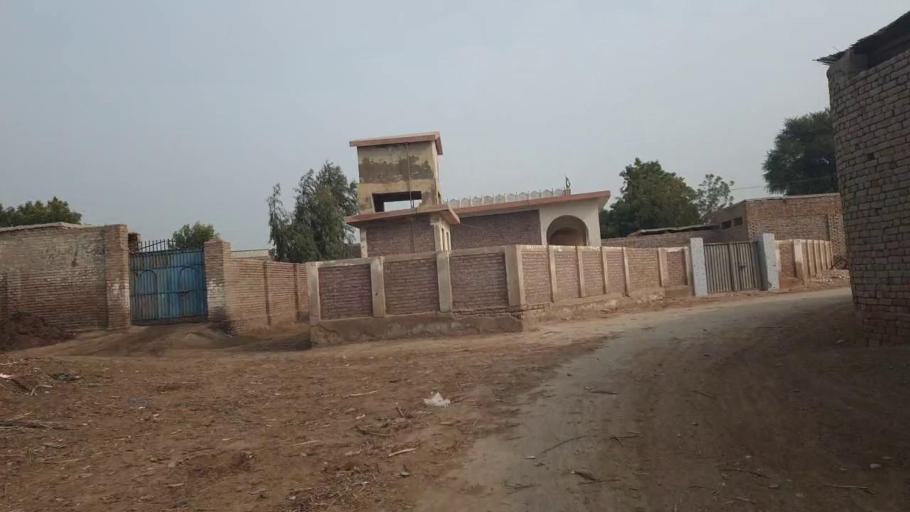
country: PK
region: Sindh
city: Shahdadpur
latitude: 25.9494
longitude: 68.7047
